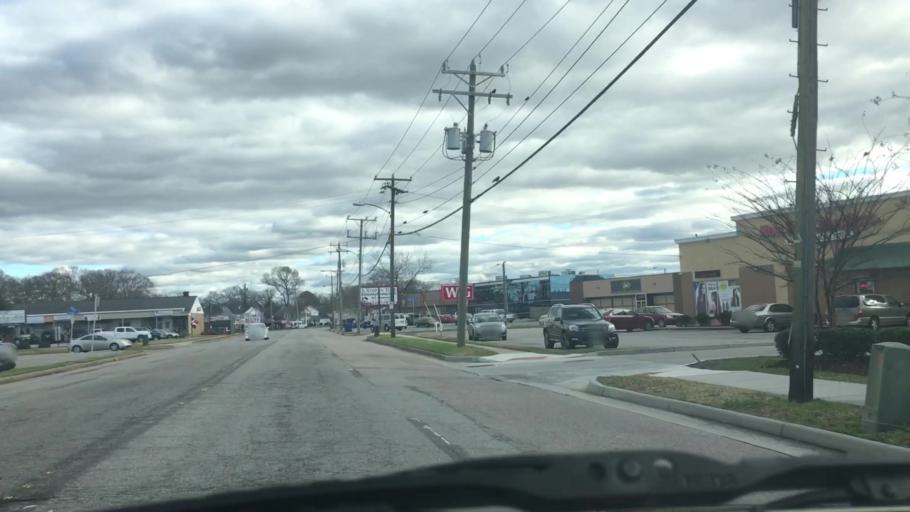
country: US
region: Virginia
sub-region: City of Norfolk
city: Norfolk
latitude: 36.9143
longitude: -76.2496
